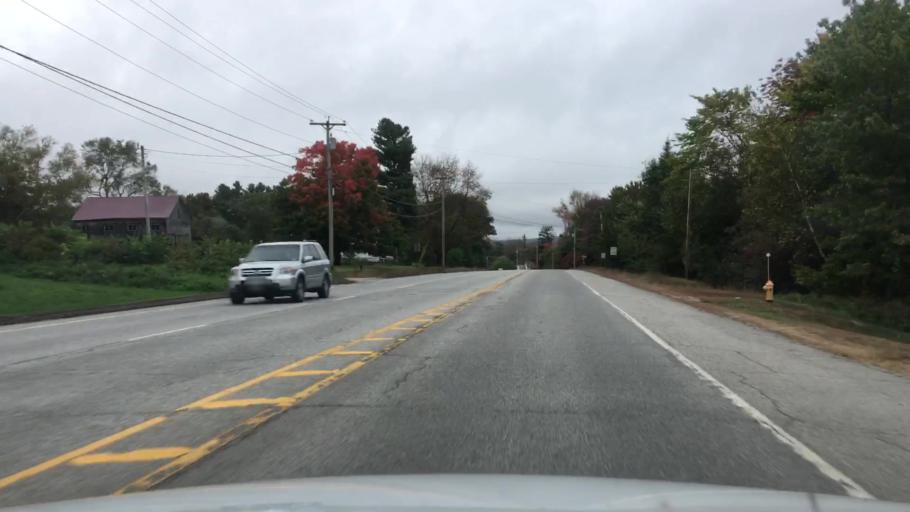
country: US
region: Maine
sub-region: Oxford County
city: Oxford
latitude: 44.1183
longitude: -70.4445
